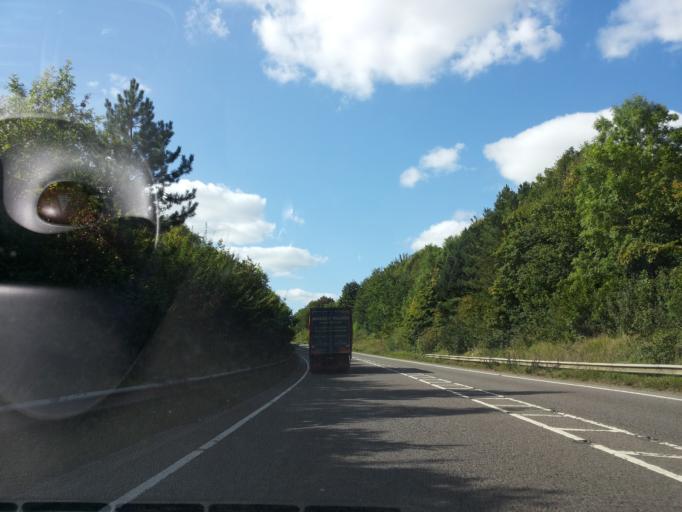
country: GB
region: England
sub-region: Wiltshire
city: Warminster
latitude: 51.1968
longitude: -2.2048
